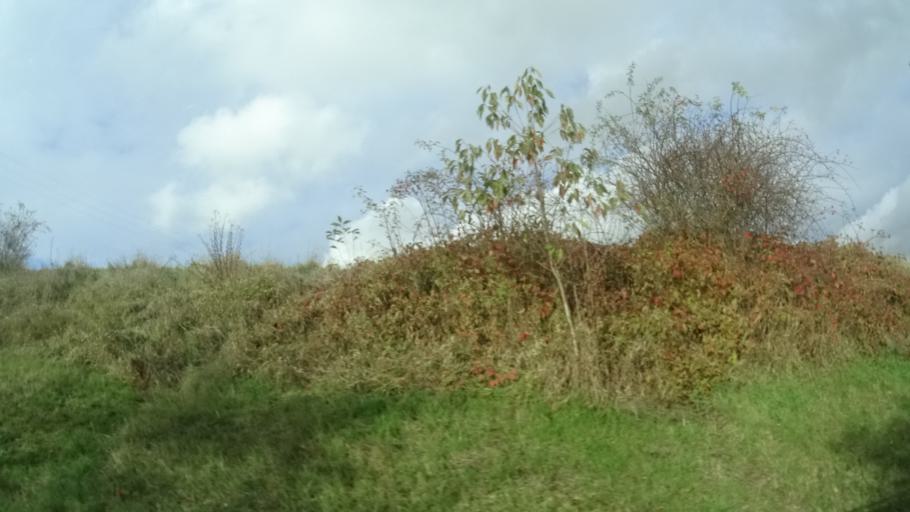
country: DE
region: Bavaria
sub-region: Regierungsbezirk Unterfranken
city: Saal an der Saale
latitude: 50.3368
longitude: 10.3786
